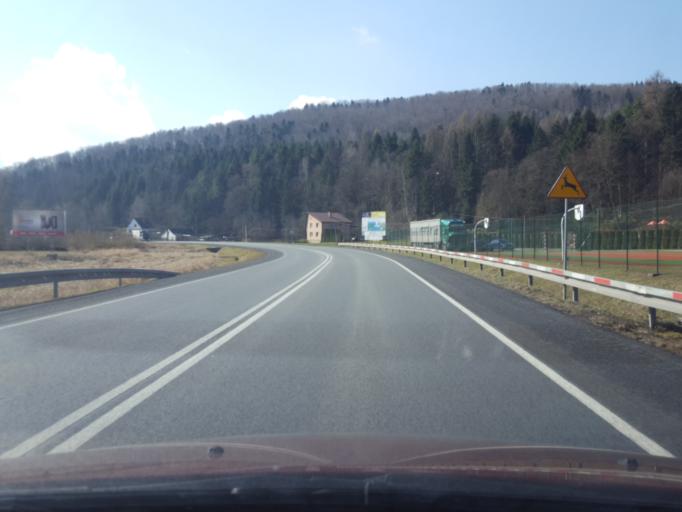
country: PL
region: Lesser Poland Voivodeship
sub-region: Powiat nowosadecki
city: Lososina Dolna
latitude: 49.7799
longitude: 20.6421
